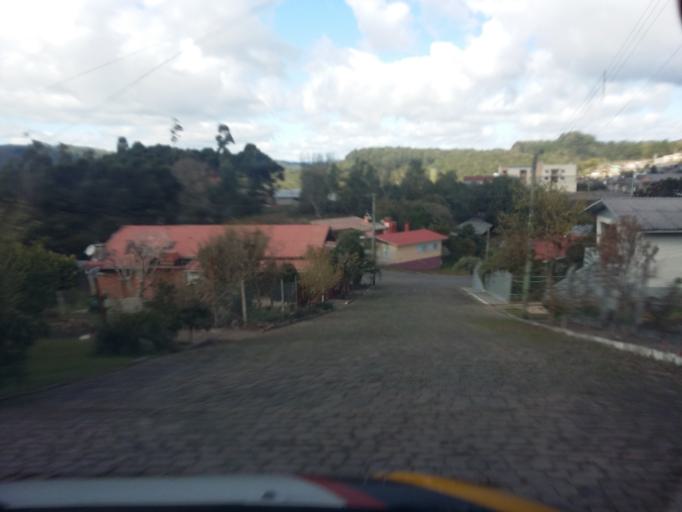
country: BR
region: Rio Grande do Sul
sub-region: Sao Marcos
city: Sao Marcos
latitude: -28.7974
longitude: -51.0925
